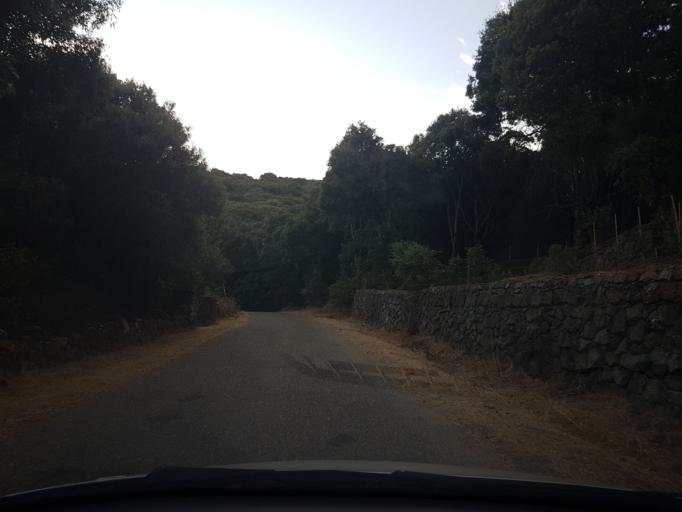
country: IT
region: Sardinia
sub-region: Provincia di Oristano
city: Seneghe
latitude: 40.1086
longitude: 8.6002
